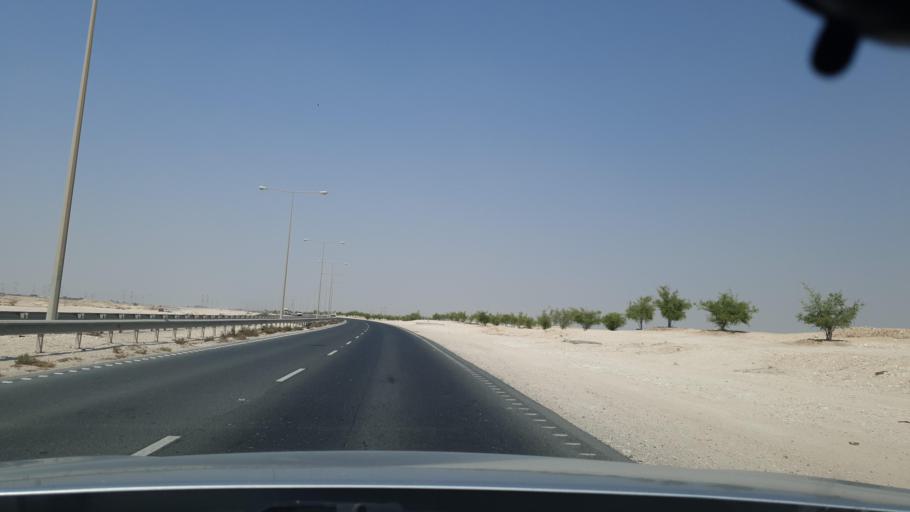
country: QA
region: Al Khawr
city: Al Khawr
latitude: 25.7348
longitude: 51.4926
